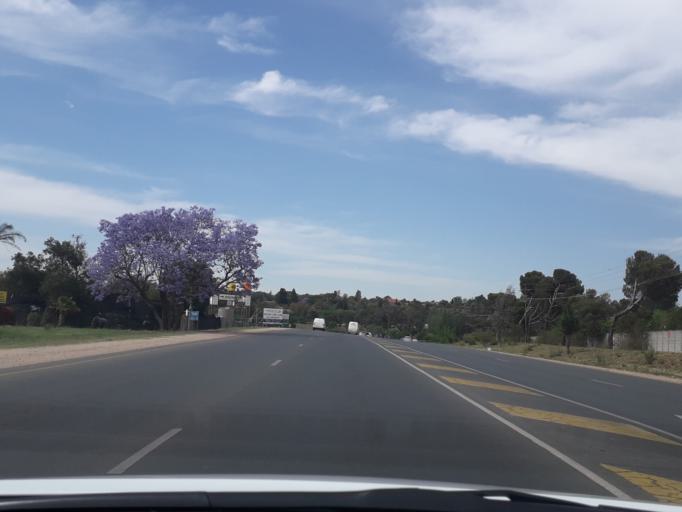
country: ZA
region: Gauteng
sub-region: City of Johannesburg Metropolitan Municipality
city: Diepsloot
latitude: -25.9898
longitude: 28.0517
